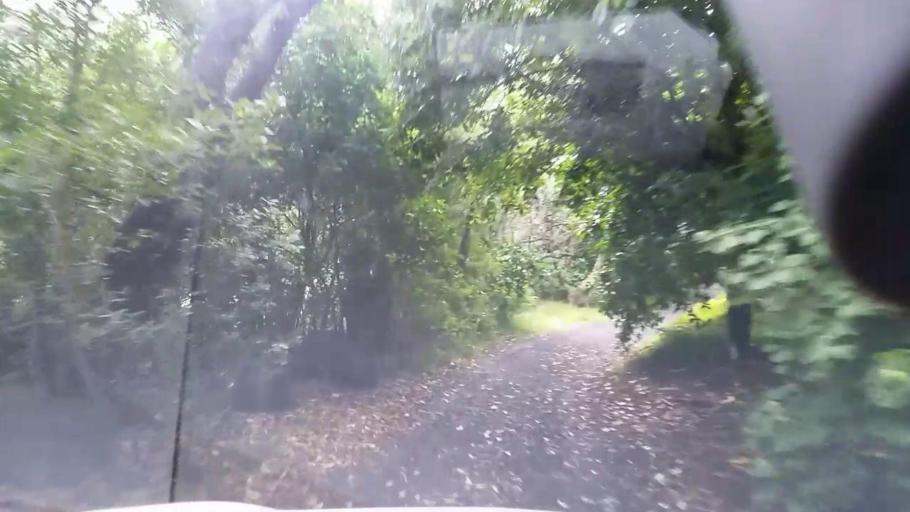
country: NZ
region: Auckland
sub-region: Auckland
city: Muriwai Beach
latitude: -36.9854
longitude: 174.4770
